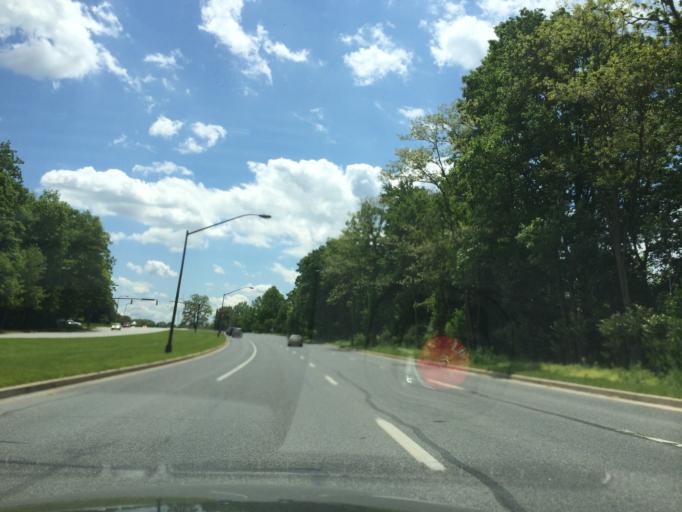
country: US
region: Maryland
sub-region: Howard County
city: Riverside
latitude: 39.1867
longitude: -76.8514
